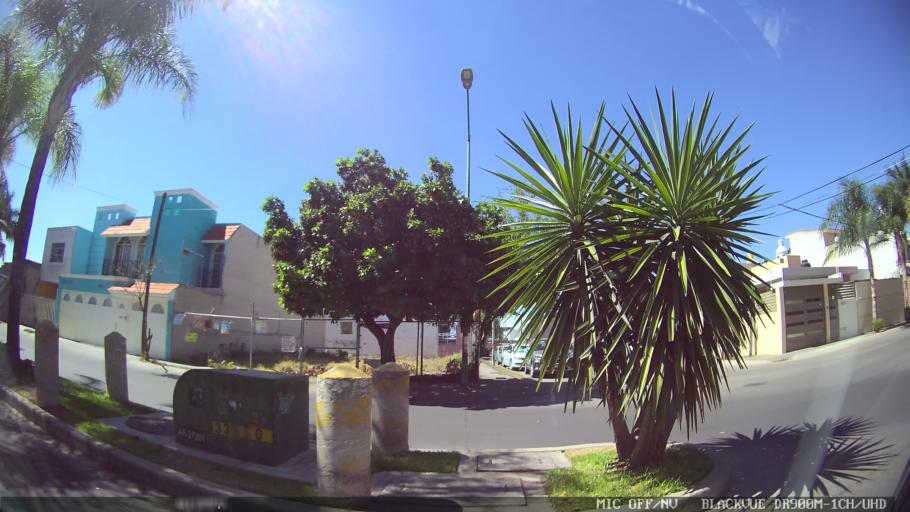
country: MX
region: Jalisco
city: Tlaquepaque
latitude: 20.6468
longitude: -103.2839
